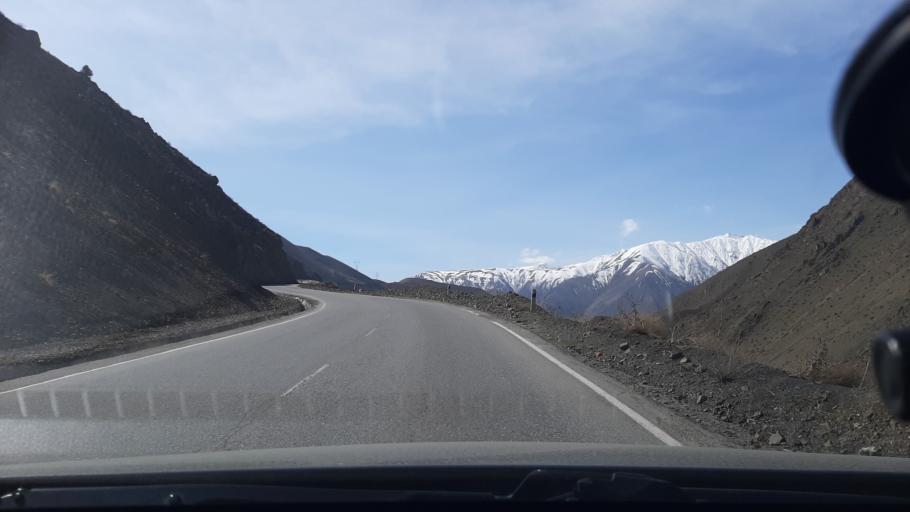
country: TJ
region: Viloyati Sughd
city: Ayni
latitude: 39.4567
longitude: 68.5461
